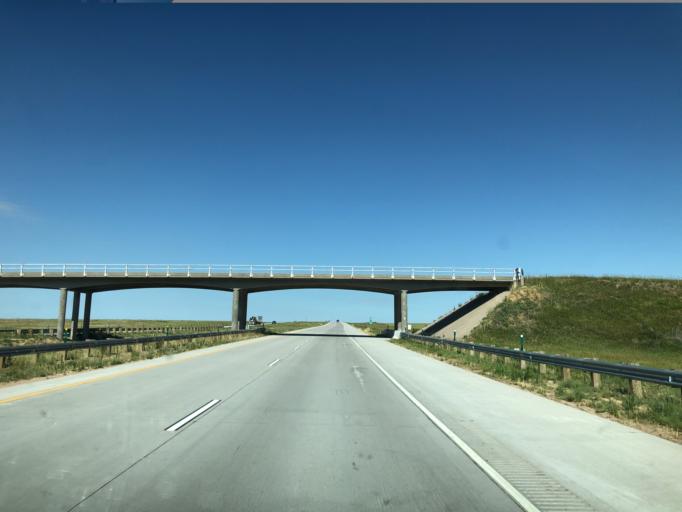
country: US
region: Colorado
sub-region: Kit Carson County
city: Burlington
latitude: 39.2944
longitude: -102.7793
